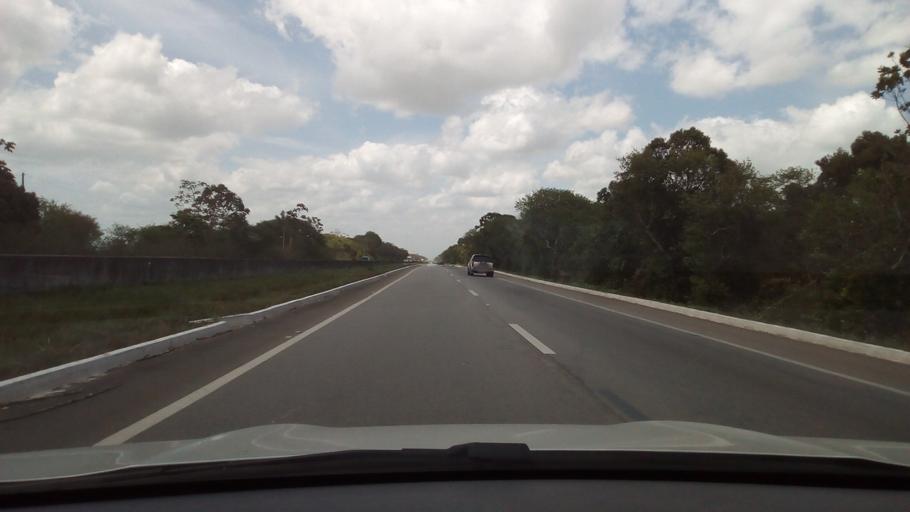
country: BR
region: Paraiba
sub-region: Mamanguape
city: Mamanguape
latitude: -6.9124
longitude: -35.1139
